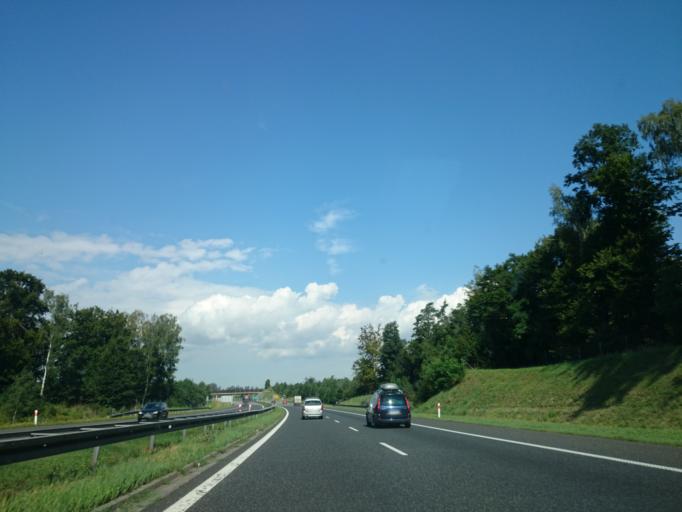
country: PL
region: Opole Voivodeship
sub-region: Powiat strzelecki
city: Ujazd
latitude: 50.4417
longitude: 18.3588
